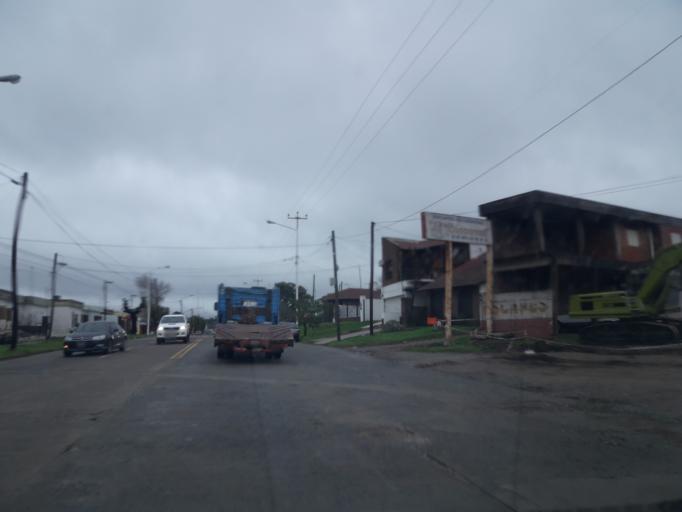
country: AR
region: Buenos Aires
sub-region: Partido de Tandil
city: Tandil
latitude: -37.3171
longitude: -59.1546
